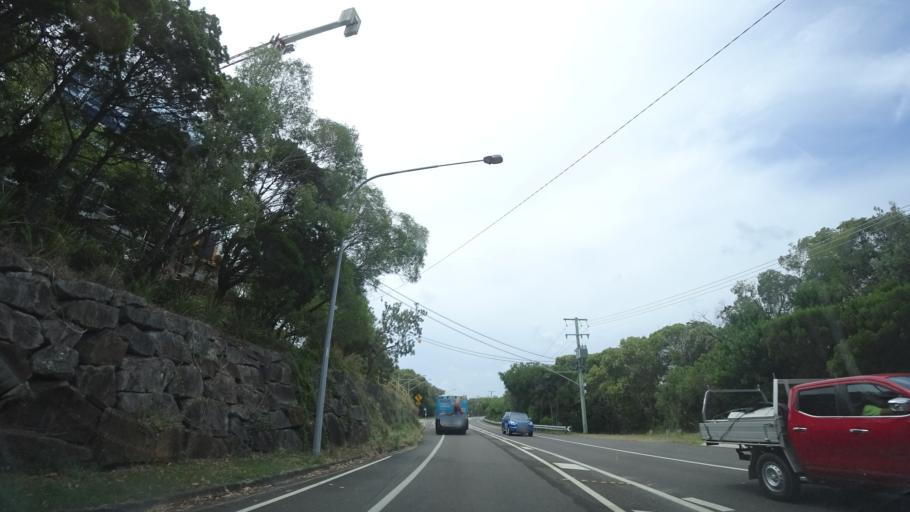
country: AU
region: Queensland
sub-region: Sunshine Coast
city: Coolum Beach
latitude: -26.5427
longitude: 153.0973
